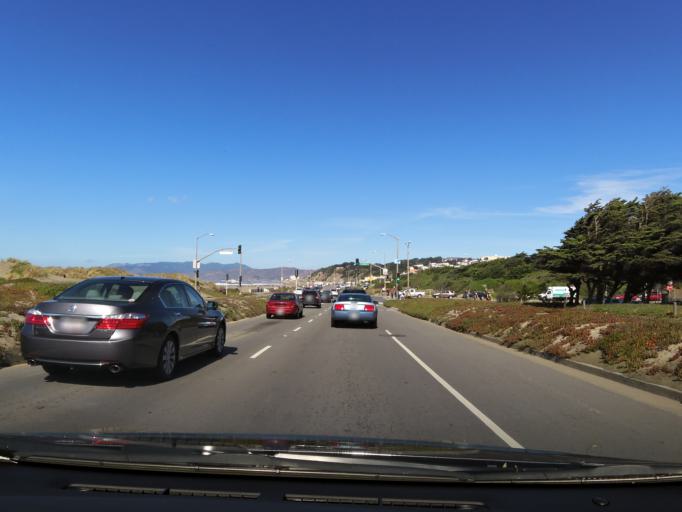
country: US
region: California
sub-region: San Mateo County
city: Daly City
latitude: 37.7632
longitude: -122.5103
